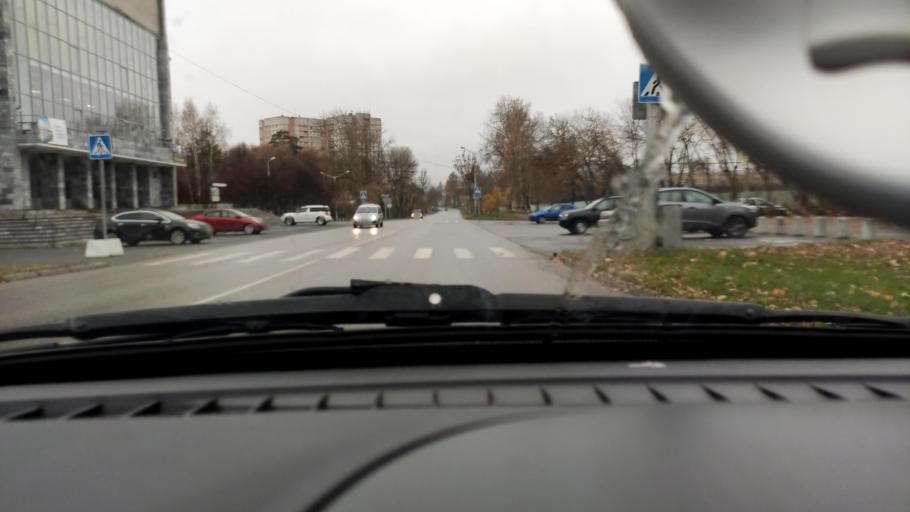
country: RU
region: Perm
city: Kultayevo
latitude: 57.9985
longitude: 55.9527
